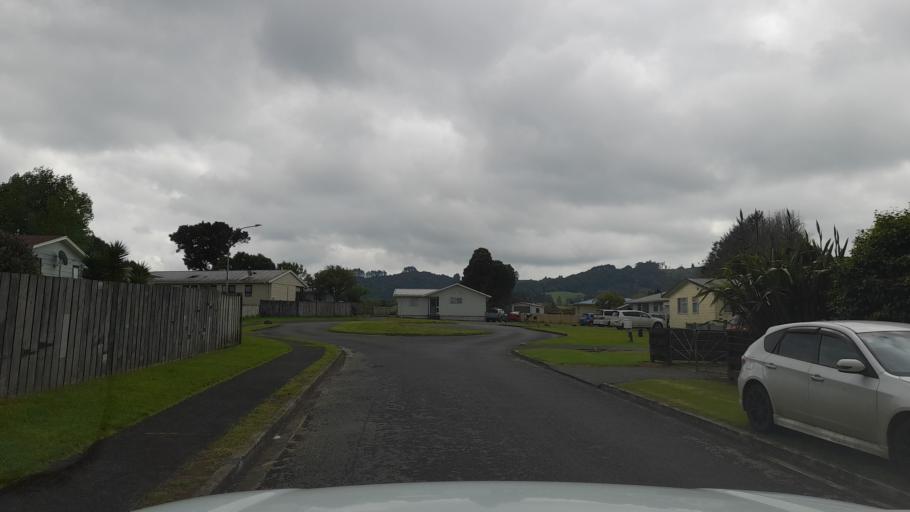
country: NZ
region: Northland
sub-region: Far North District
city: Waimate North
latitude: -35.4019
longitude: 173.7973
